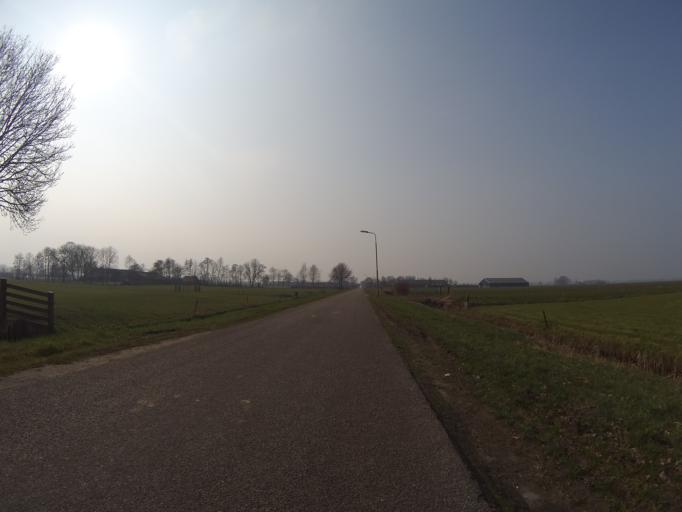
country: NL
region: Utrecht
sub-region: Gemeente Amersfoort
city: Hoogland
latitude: 52.1984
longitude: 5.3477
